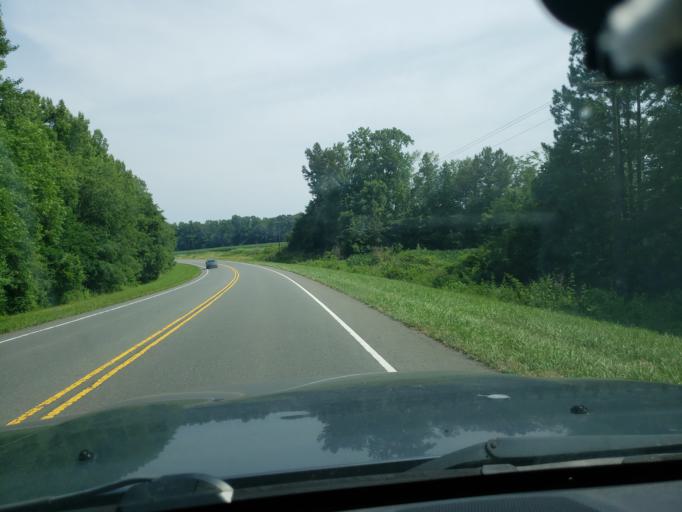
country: US
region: North Carolina
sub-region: Alamance County
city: Saxapahaw
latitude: 35.9491
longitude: -79.2526
